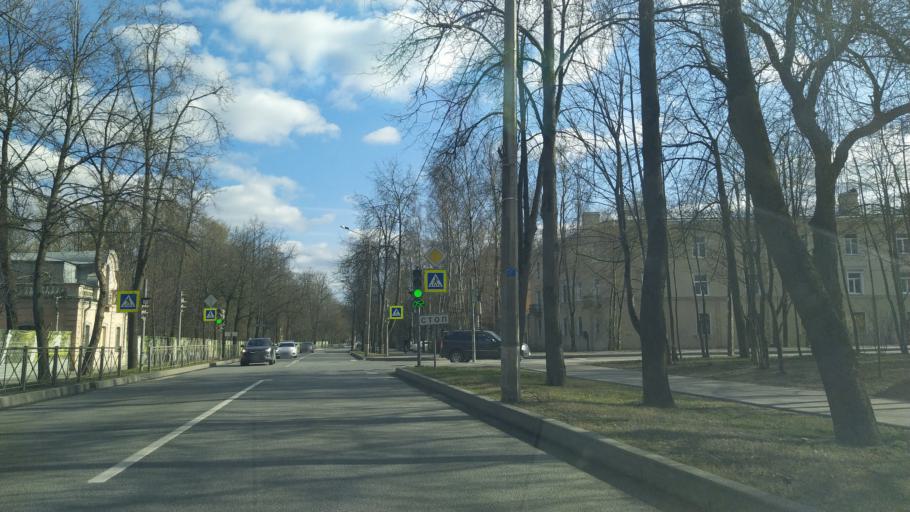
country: RU
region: St.-Petersburg
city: Pushkin
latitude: 59.7091
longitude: 30.4141
